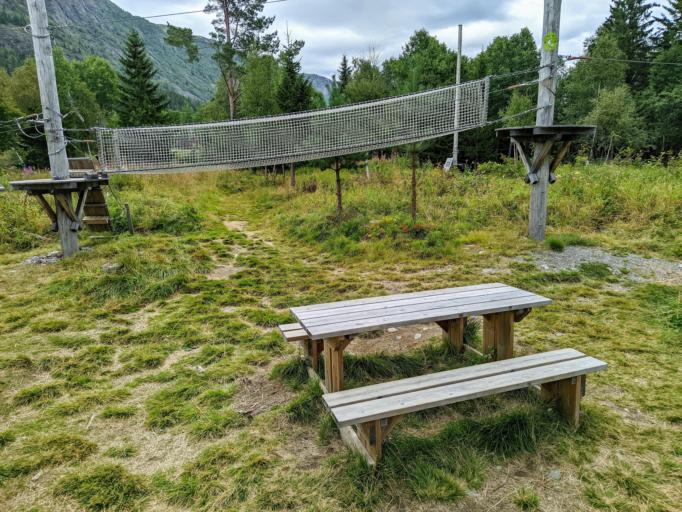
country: NO
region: Buskerud
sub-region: Hemsedal
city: Hemsedal
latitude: 60.8617
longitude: 8.5564
